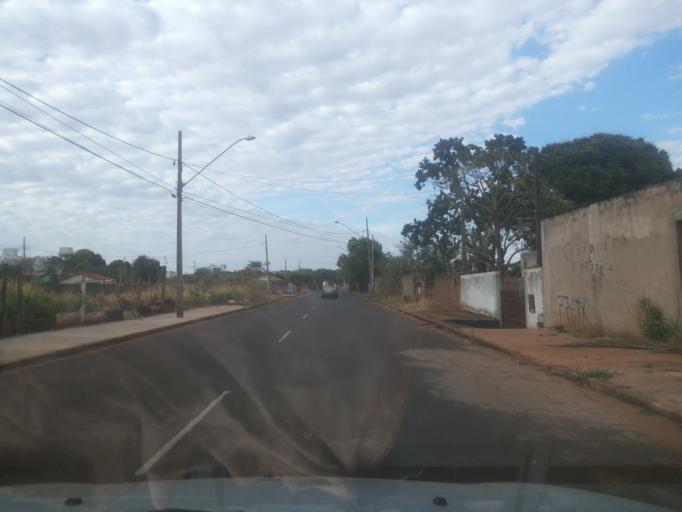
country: BR
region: Minas Gerais
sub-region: Ituiutaba
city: Ituiutaba
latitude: -18.9995
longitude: -49.4558
